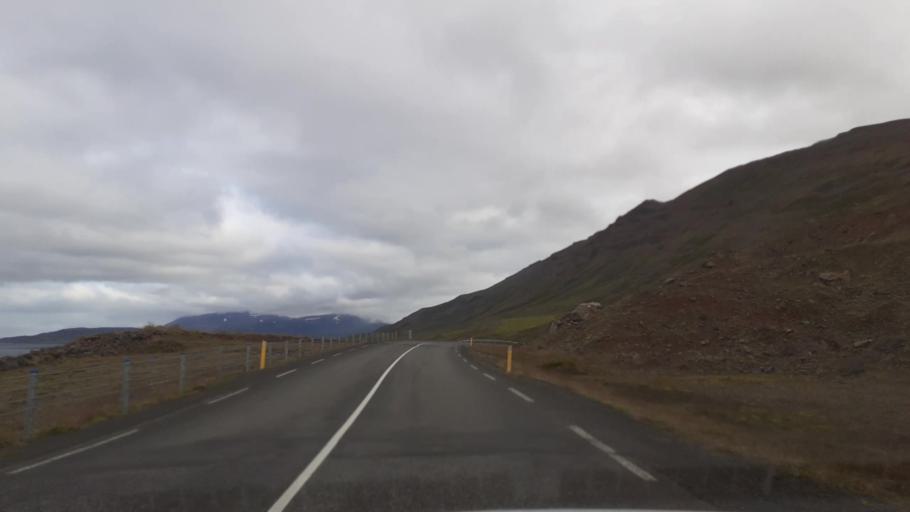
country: IS
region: Northeast
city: Akureyri
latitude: 65.8334
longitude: -18.0563
